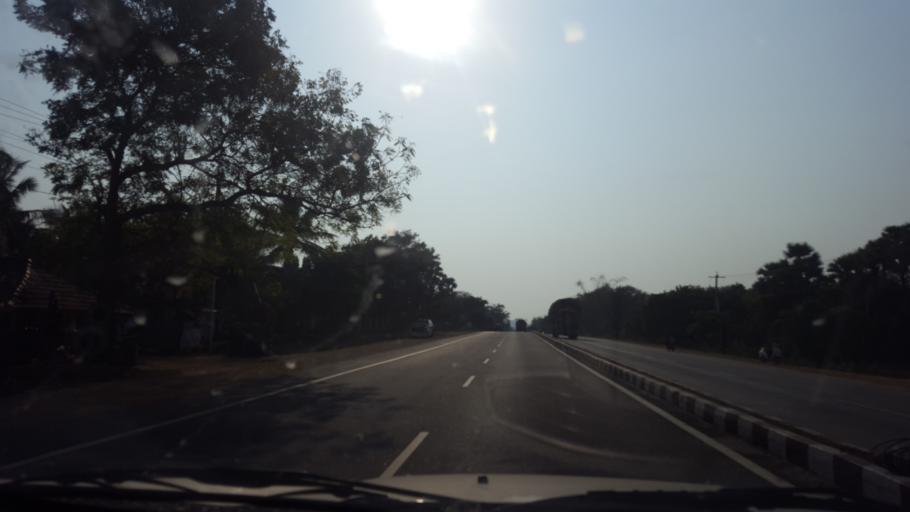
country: IN
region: Andhra Pradesh
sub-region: Vishakhapatnam
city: Etikoppaka
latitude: 17.4032
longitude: 82.6946
